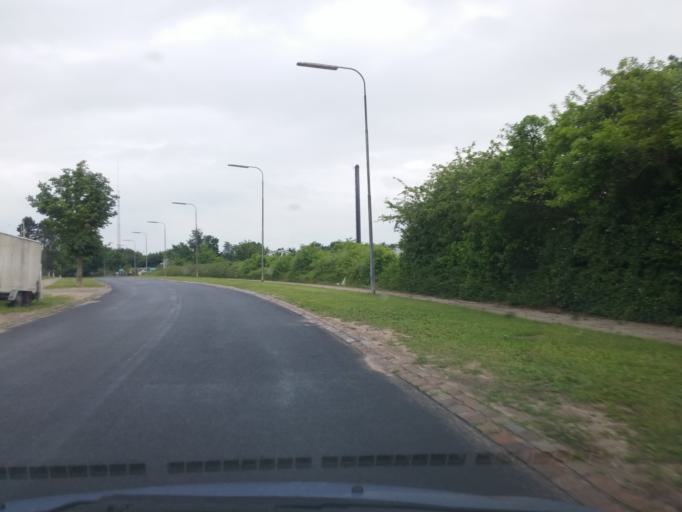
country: DK
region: South Denmark
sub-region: Odense Kommune
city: Odense
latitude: 55.4044
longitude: 10.4158
